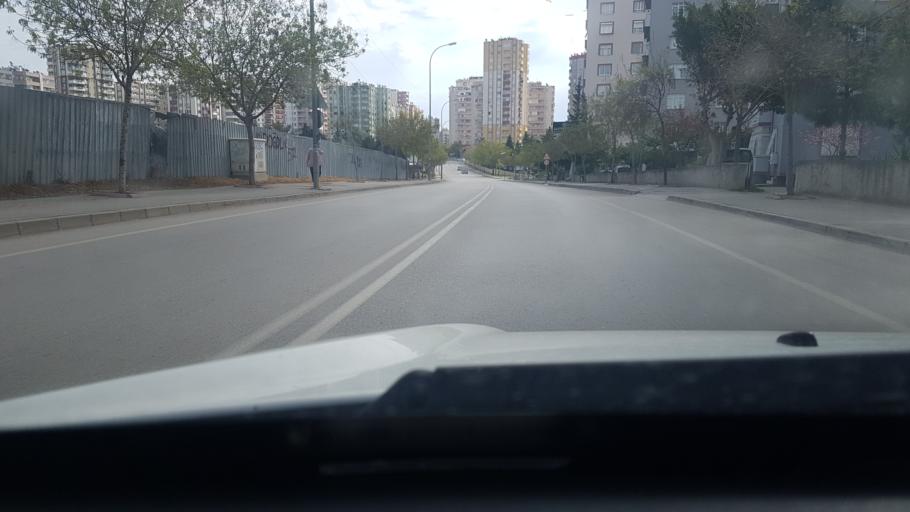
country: TR
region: Adana
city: Seyhan
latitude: 37.0345
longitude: 35.2777
